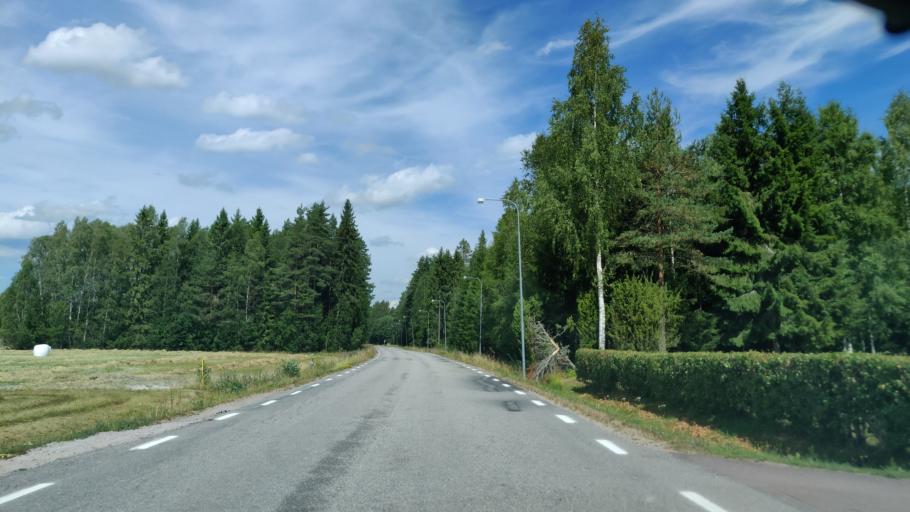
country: SE
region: Vaermland
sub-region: Hagfors Kommun
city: Ekshaerad
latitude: 60.1108
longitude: 13.5016
